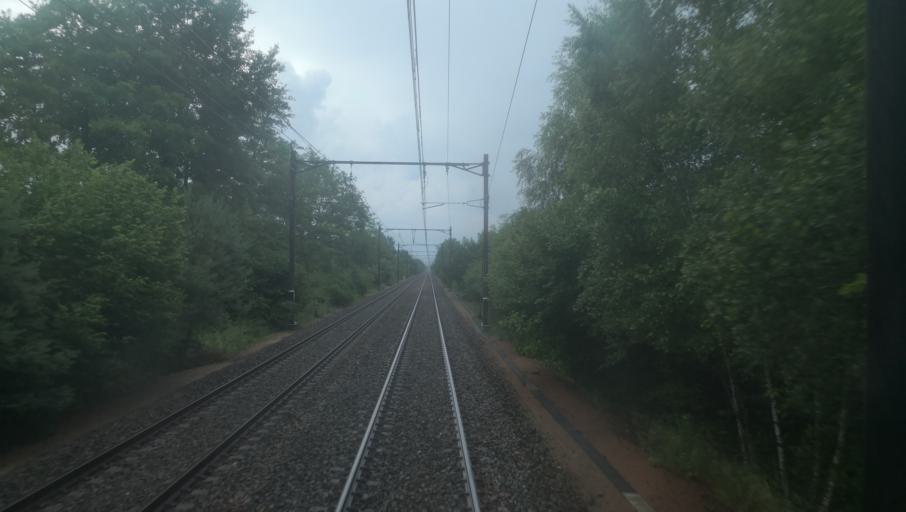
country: FR
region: Centre
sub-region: Departement du Loiret
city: Saint-Cyr-en-Val
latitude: 47.7897
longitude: 1.9419
